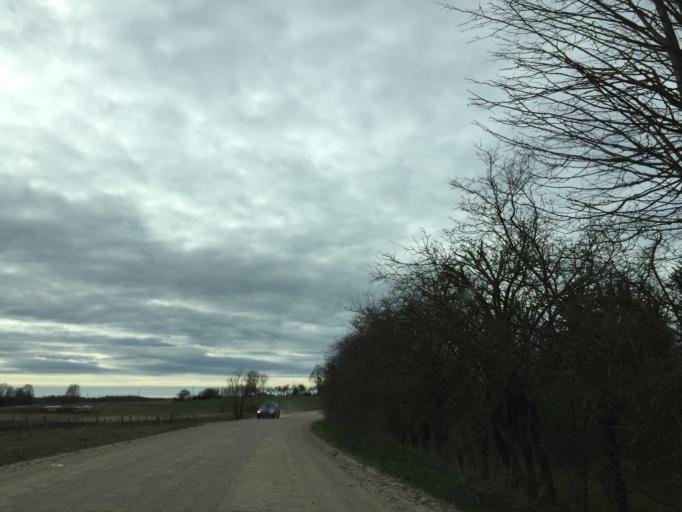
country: LT
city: Silale
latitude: 55.6191
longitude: 22.2112
